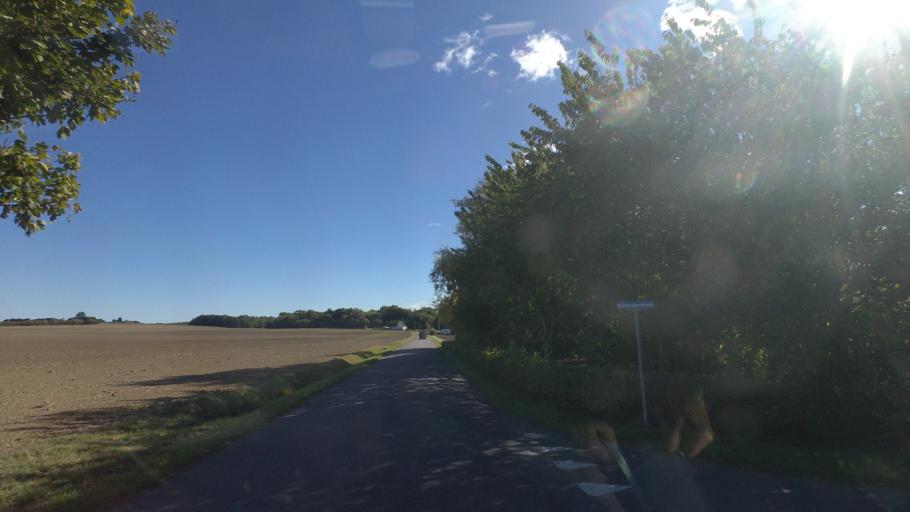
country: DK
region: Capital Region
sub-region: Bornholm Kommune
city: Akirkeby
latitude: 55.1354
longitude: 15.0188
